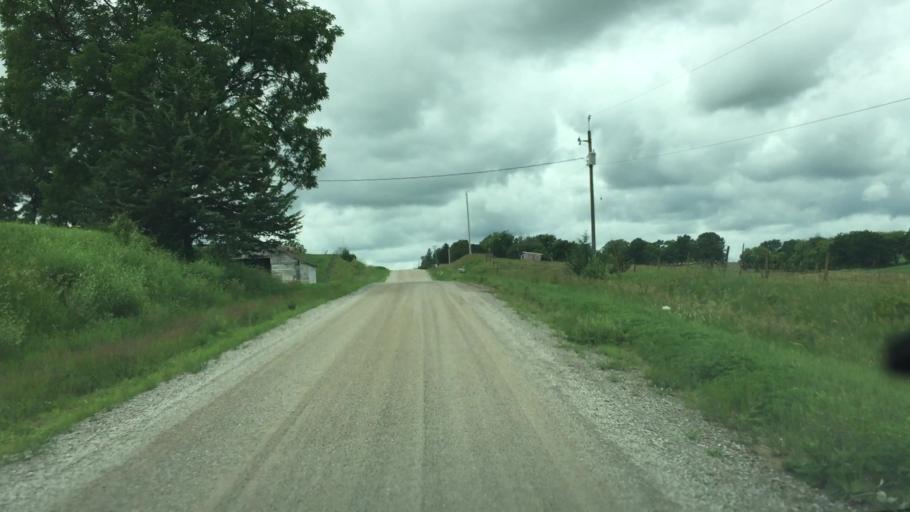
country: US
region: Iowa
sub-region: Jasper County
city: Prairie City
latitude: 41.6010
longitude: -93.1460
